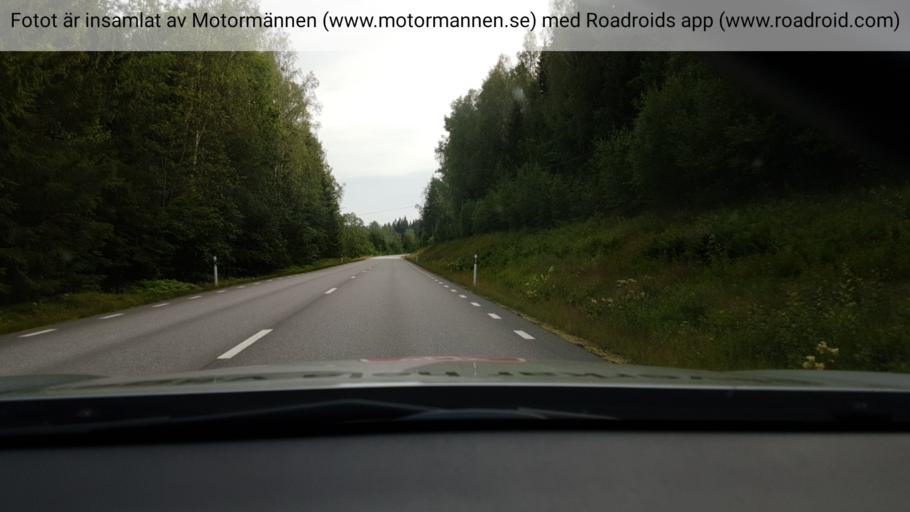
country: SE
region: Vaestra Goetaland
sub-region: Bengtsfors Kommun
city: Dals Langed
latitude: 59.0463
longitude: 12.4316
